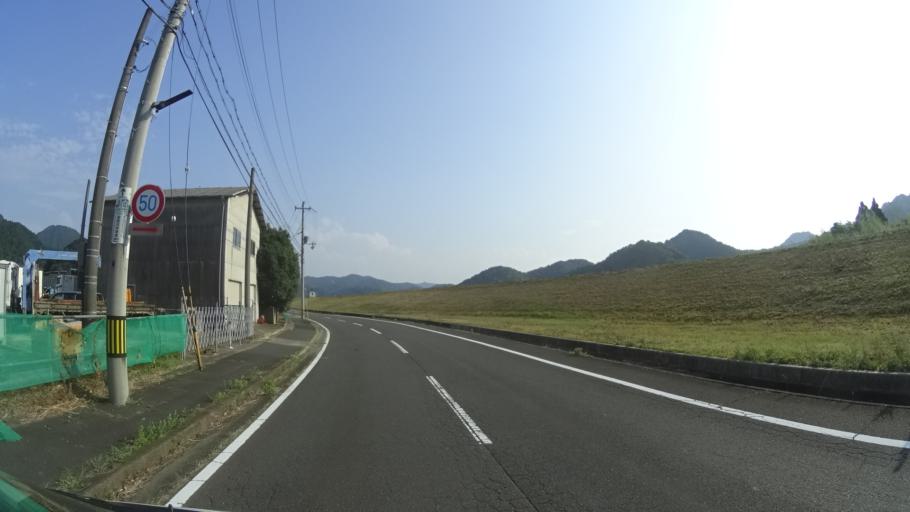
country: JP
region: Kyoto
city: Maizuru
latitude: 35.4732
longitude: 135.2815
